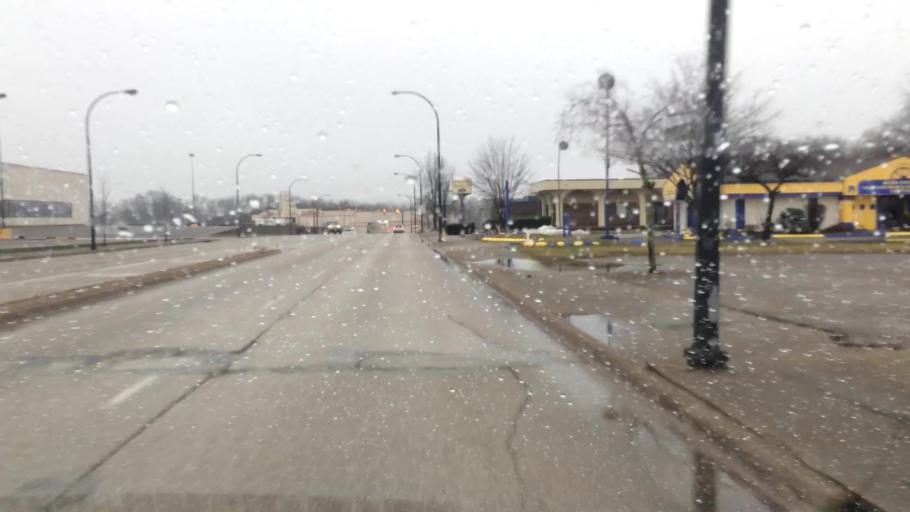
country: US
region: Ohio
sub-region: Summit County
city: Cuyahoga Falls
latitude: 41.1127
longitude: -81.4715
